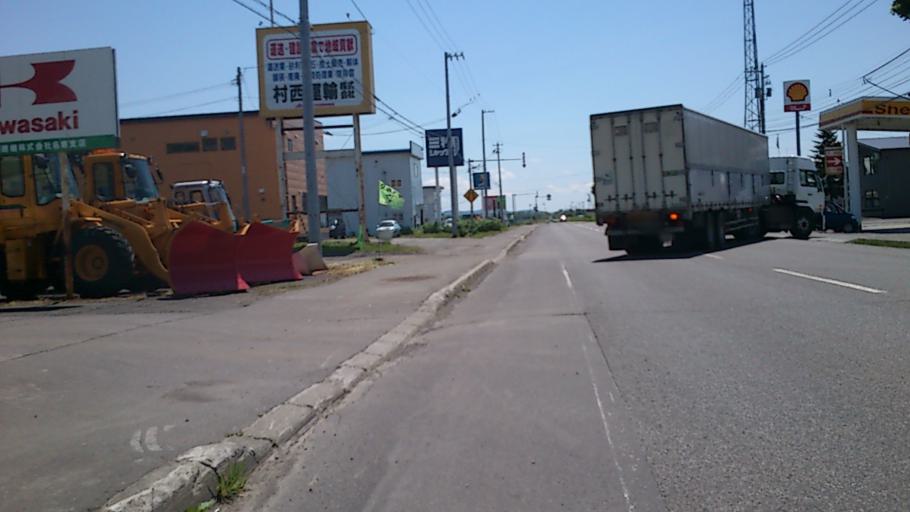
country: JP
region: Hokkaido
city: Nayoro
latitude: 44.3242
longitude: 142.4575
